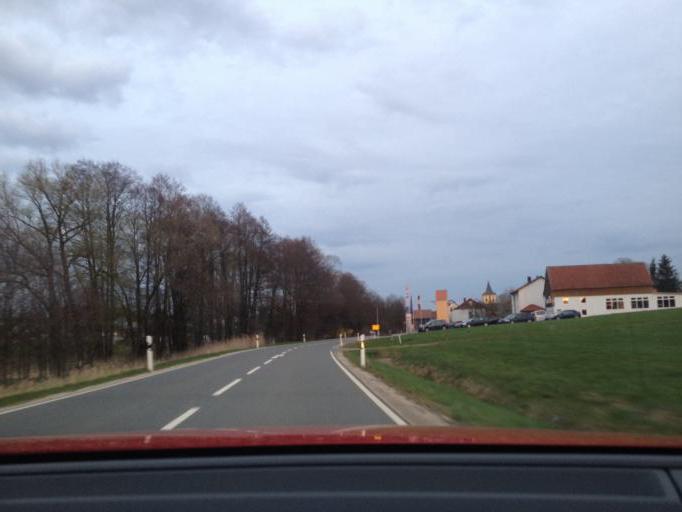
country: DE
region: Bavaria
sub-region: Upper Palatinate
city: Speinshart
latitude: 49.7769
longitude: 11.8076
